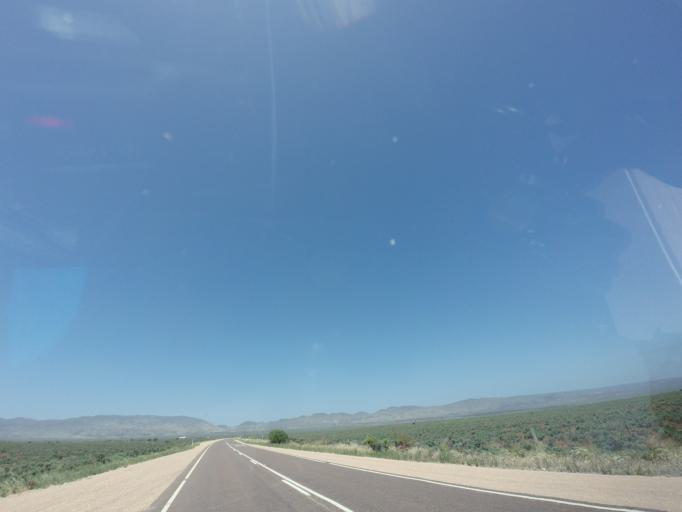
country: AU
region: South Australia
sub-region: Port Augusta
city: Port Augusta
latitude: -32.6267
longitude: 137.9208
